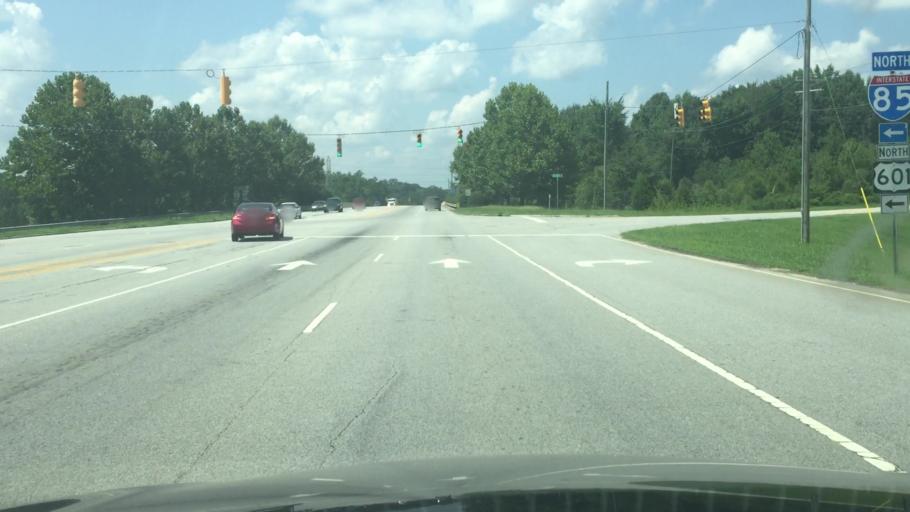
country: US
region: North Carolina
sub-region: Rowan County
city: Salisbury
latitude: 35.6329
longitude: -80.4885
